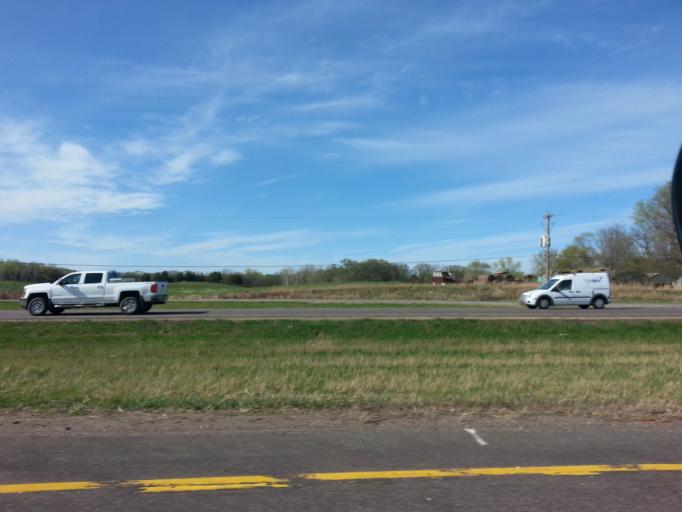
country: US
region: Minnesota
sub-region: Washington County
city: Lake Elmo
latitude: 45.0355
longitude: -92.9055
